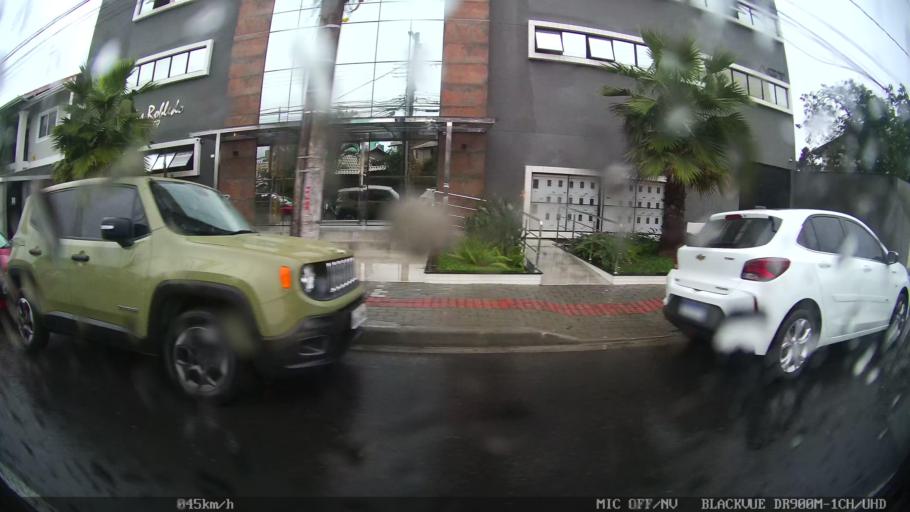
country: BR
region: Santa Catarina
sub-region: Itajai
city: Itajai
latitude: -26.9137
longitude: -48.6700
